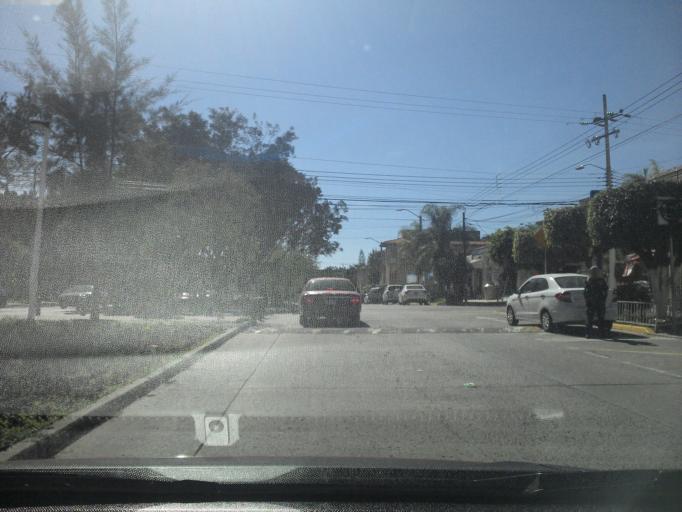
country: MX
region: Jalisco
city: Zapopan2
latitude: 20.7452
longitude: -103.4043
